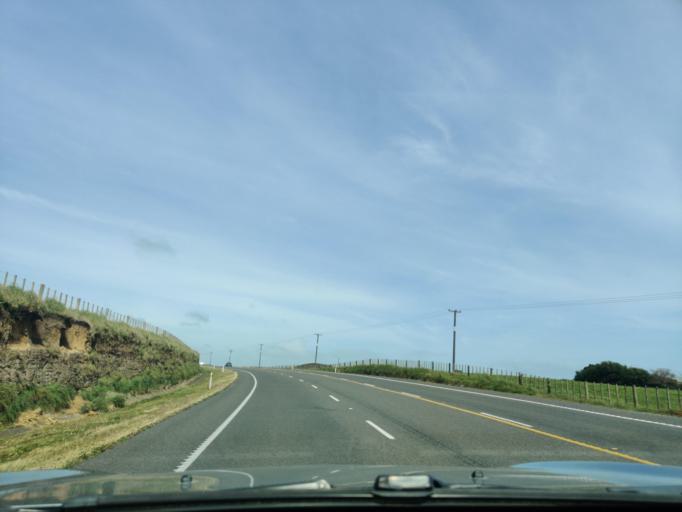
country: NZ
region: Taranaki
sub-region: South Taranaki District
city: Patea
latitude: -39.6893
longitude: 174.4216
